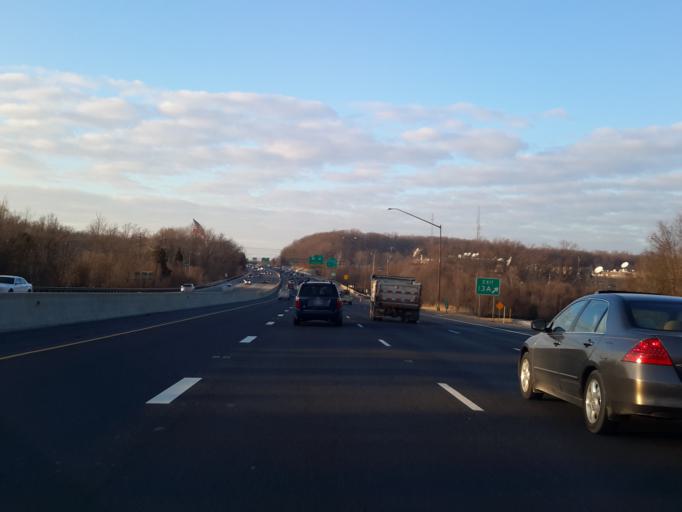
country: US
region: Maryland
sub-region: Montgomery County
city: Germantown
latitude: 39.1731
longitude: -77.2454
